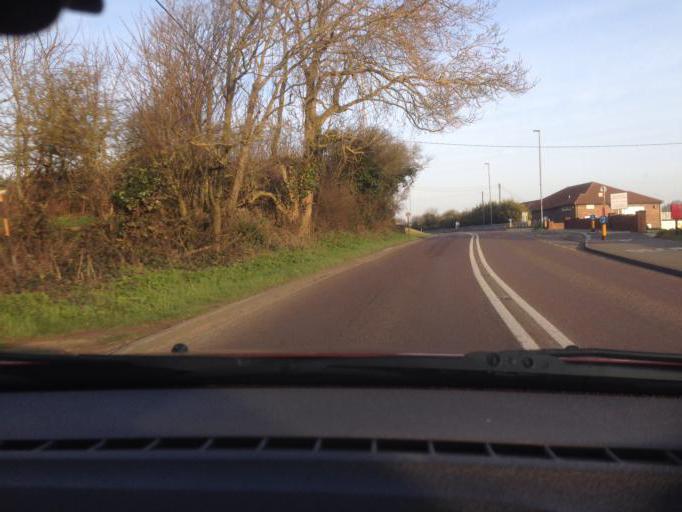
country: GB
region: England
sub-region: East Sussex
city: Newhaven
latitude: 50.7896
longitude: 0.0319
